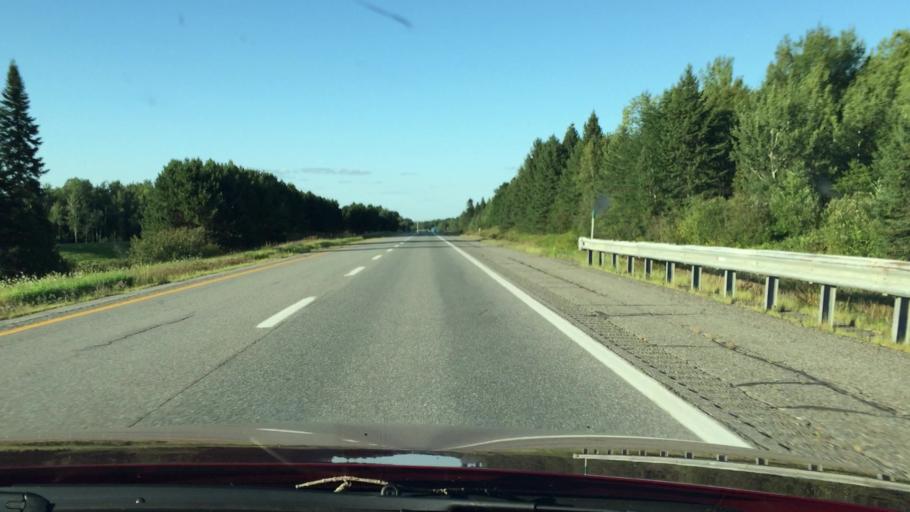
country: US
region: Maine
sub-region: Penobscot County
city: Patten
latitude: 45.8594
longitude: -68.4212
